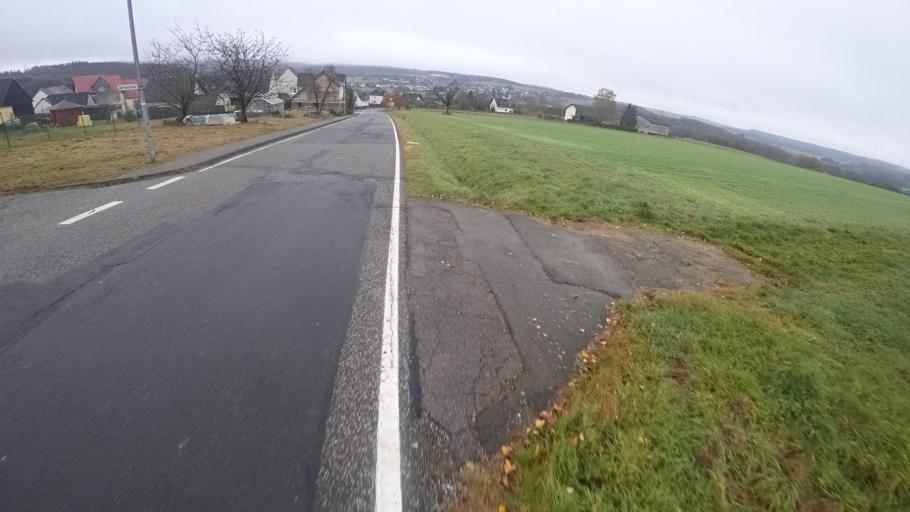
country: DE
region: Rheinland-Pfalz
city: Norath
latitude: 50.1252
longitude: 7.5762
